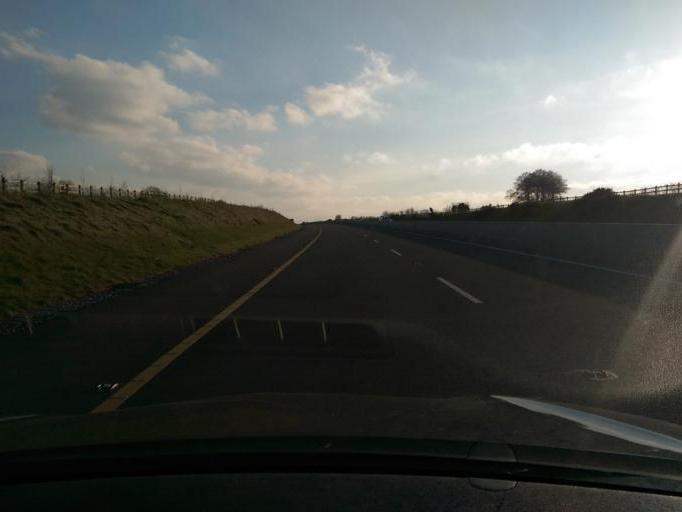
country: IE
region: Munster
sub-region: North Tipperary
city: Roscrea
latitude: 52.8987
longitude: -7.9056
